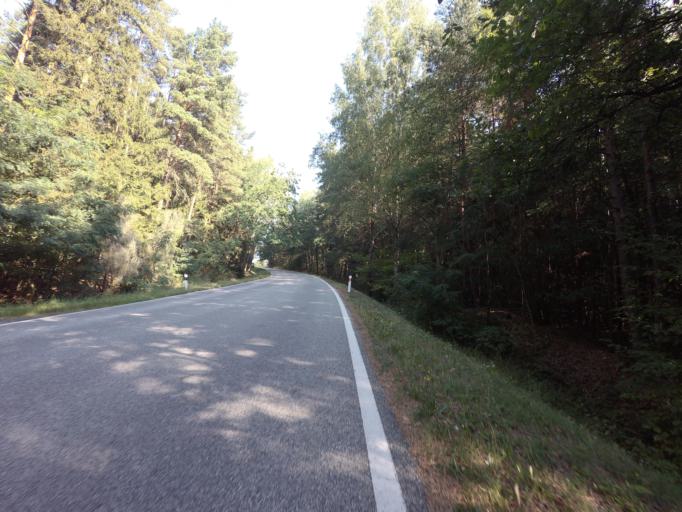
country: CZ
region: Jihocesky
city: Tyn nad Vltavou
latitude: 49.2680
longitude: 14.4100
